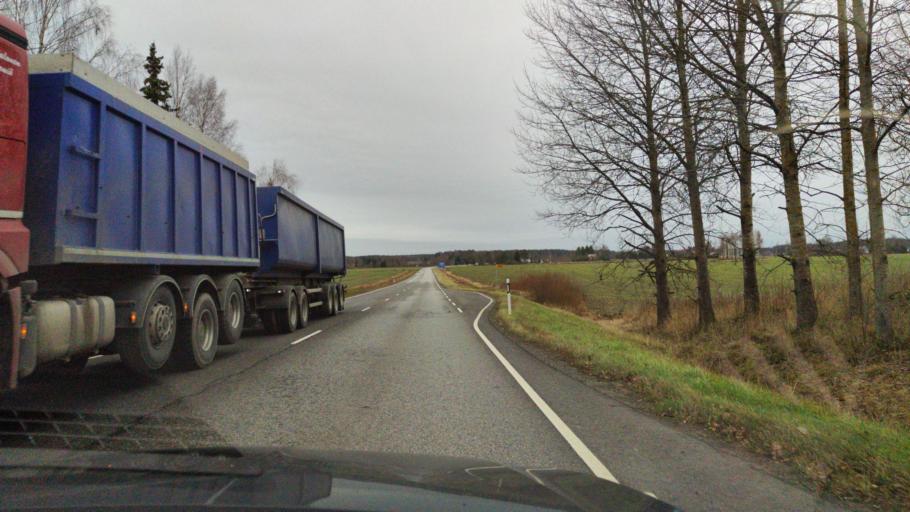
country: FI
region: Varsinais-Suomi
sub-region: Loimaa
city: Ylaene
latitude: 60.8698
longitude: 22.4044
